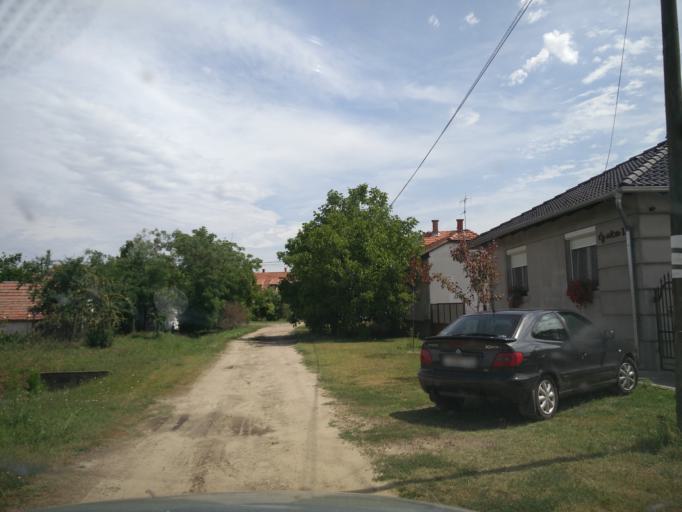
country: HU
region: Csongrad
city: Sandorfalva
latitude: 46.3704
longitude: 20.1053
